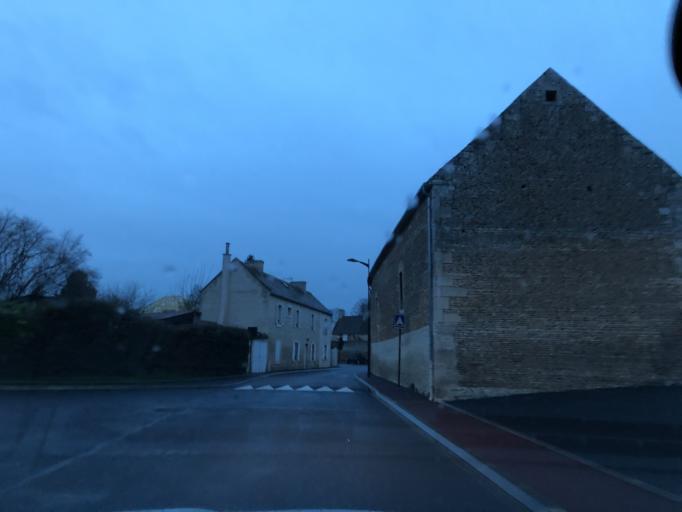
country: FR
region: Lower Normandy
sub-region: Departement du Calvados
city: Mathieu
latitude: 49.2510
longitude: -0.3653
